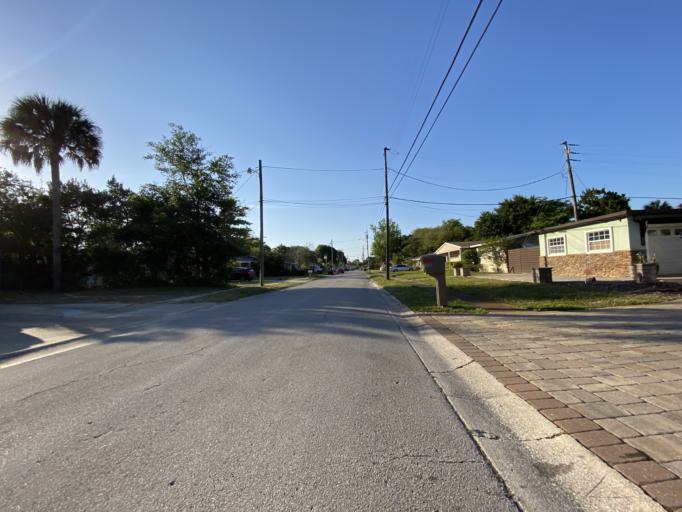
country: US
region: Florida
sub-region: Volusia County
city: South Daytona
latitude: 29.1680
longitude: -81.0035
